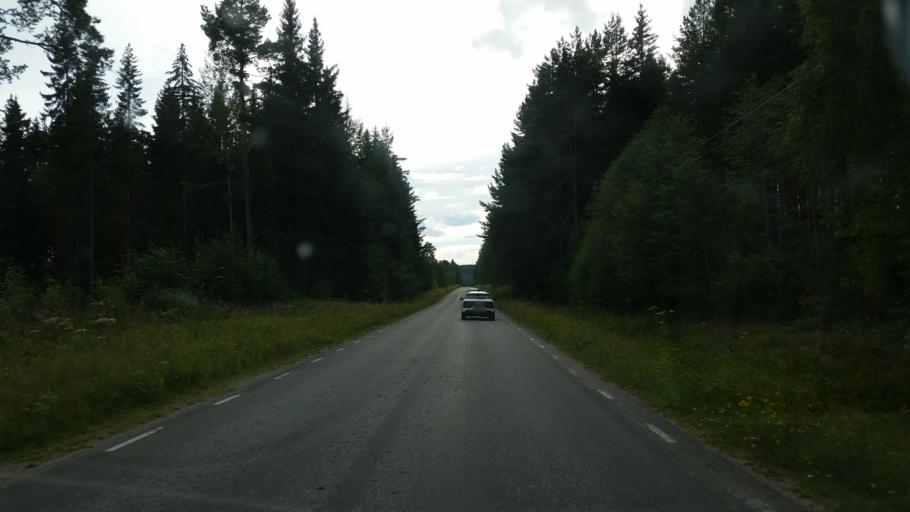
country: SE
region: Gaevleborg
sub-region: Hudiksvalls Kommun
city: Delsbo
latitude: 61.9097
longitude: 16.5716
